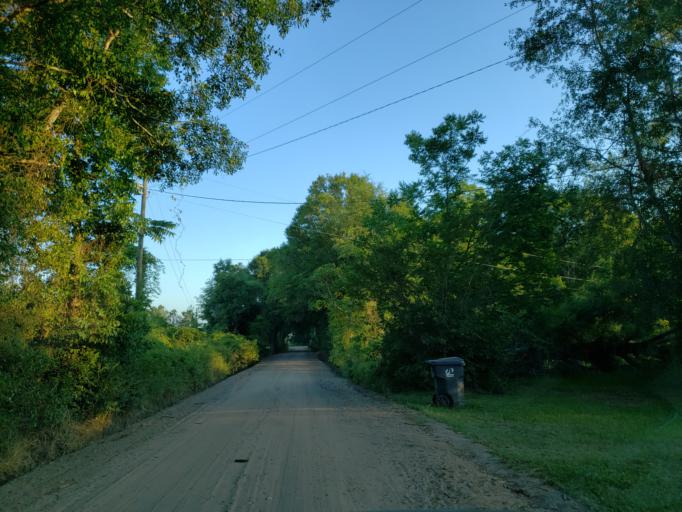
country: US
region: Georgia
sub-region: Crisp County
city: Cordele
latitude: 32.0276
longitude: -83.7484
